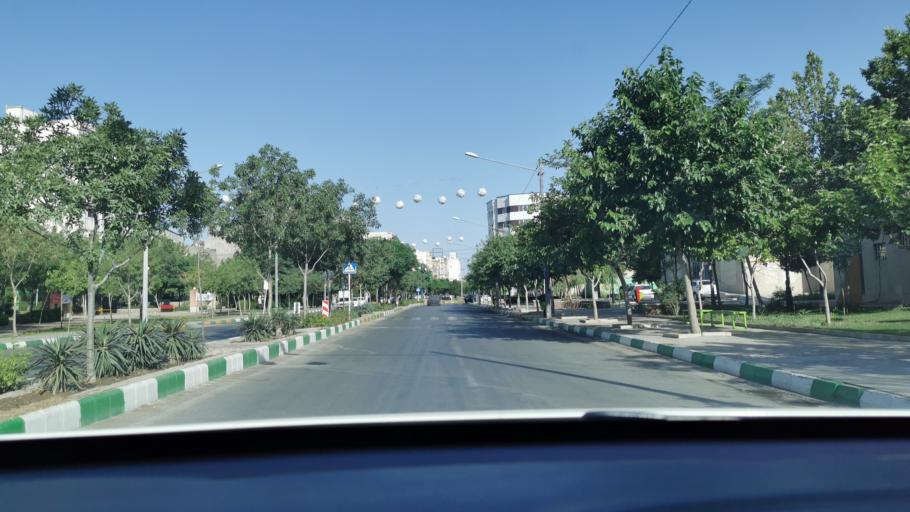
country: IR
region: Razavi Khorasan
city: Mashhad
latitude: 36.3384
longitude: 59.5085
